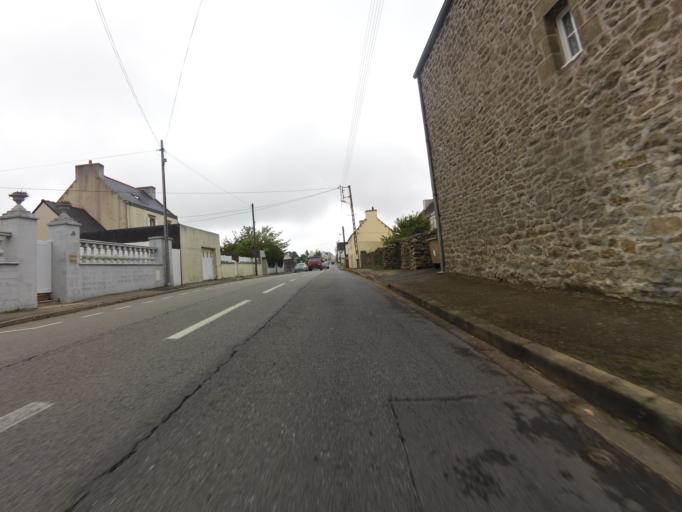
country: FR
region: Brittany
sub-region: Departement du Finistere
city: Plouhinec
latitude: 48.0156
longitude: -4.4975
